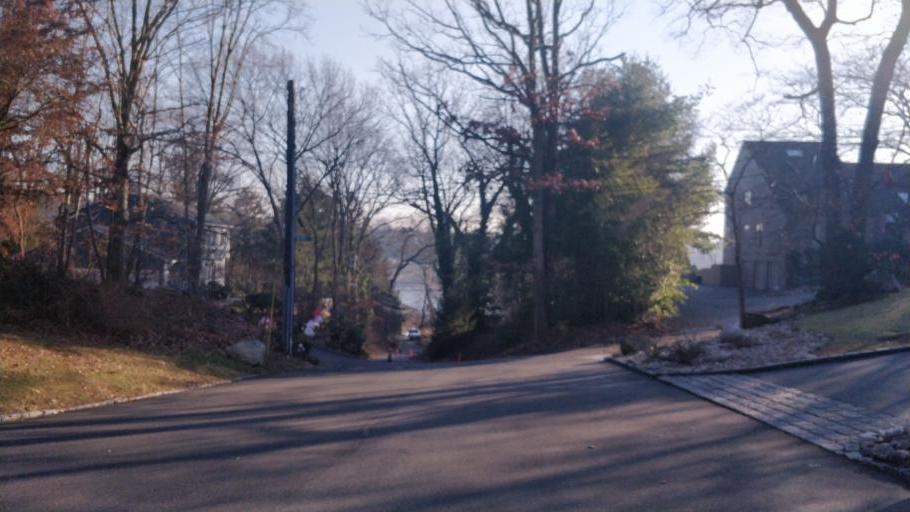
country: US
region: New York
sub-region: Nassau County
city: Bayville
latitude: 40.9016
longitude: -73.5661
